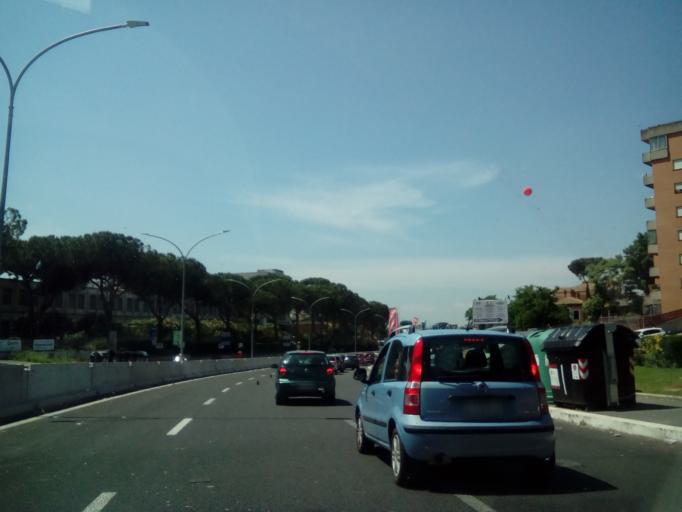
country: IT
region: Latium
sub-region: Citta metropolitana di Roma Capitale
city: Colle Verde
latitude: 41.9296
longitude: 12.5772
